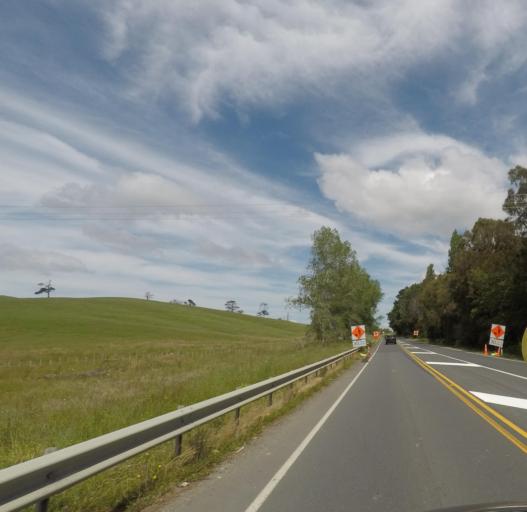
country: NZ
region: Auckland
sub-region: Auckland
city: Rothesay Bay
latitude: -36.6657
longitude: 174.6784
